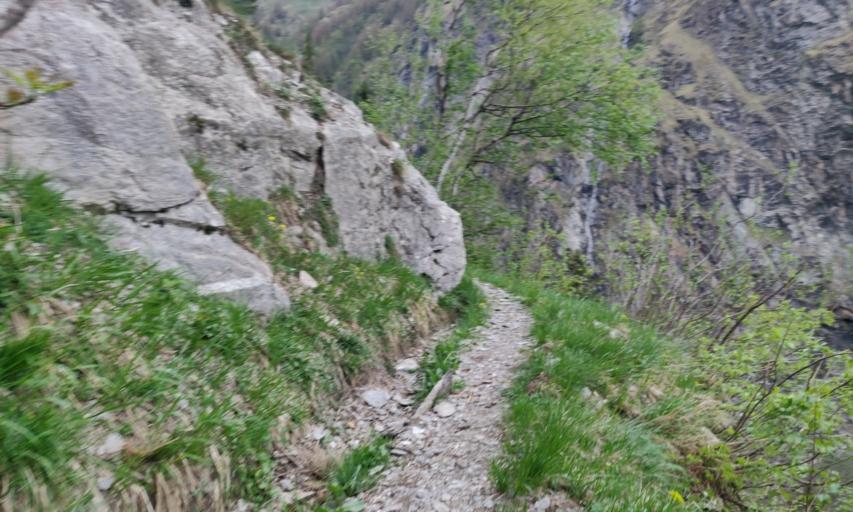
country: CH
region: Valais
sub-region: Visp District
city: Baltschieder
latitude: 46.3292
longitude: 7.8779
